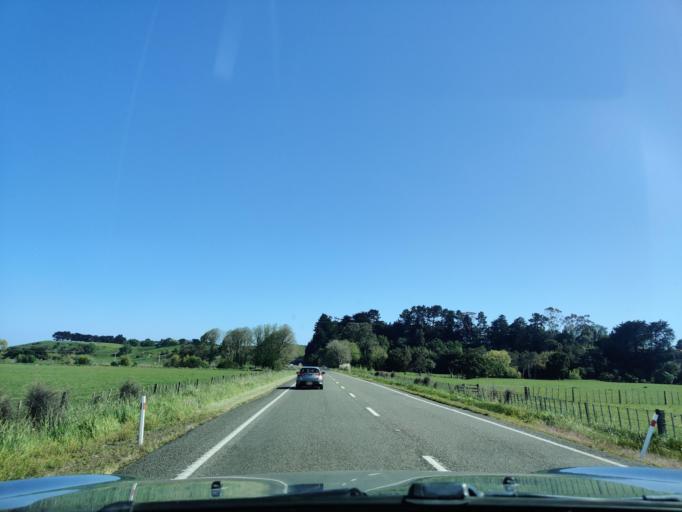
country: NZ
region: Manawatu-Wanganui
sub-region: Rangitikei District
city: Bulls
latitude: -40.0641
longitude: 175.2235
